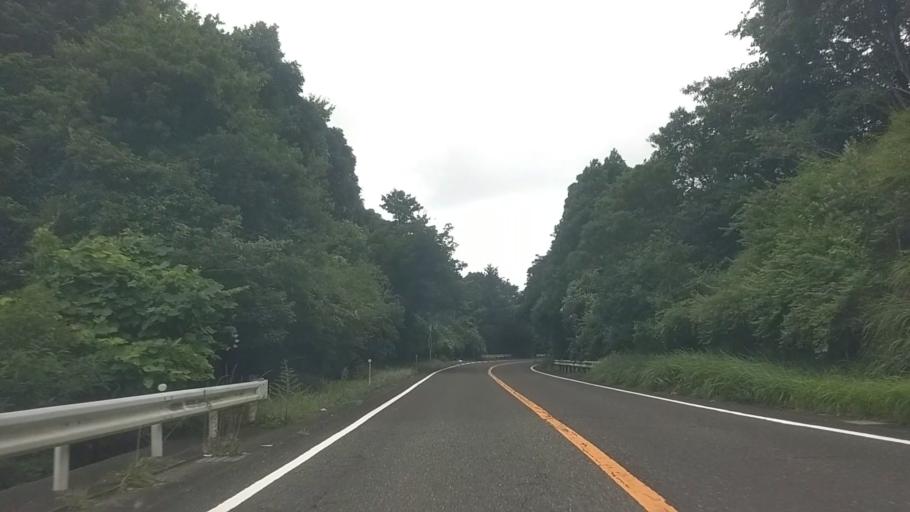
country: JP
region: Chiba
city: Kawaguchi
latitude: 35.2154
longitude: 140.0479
